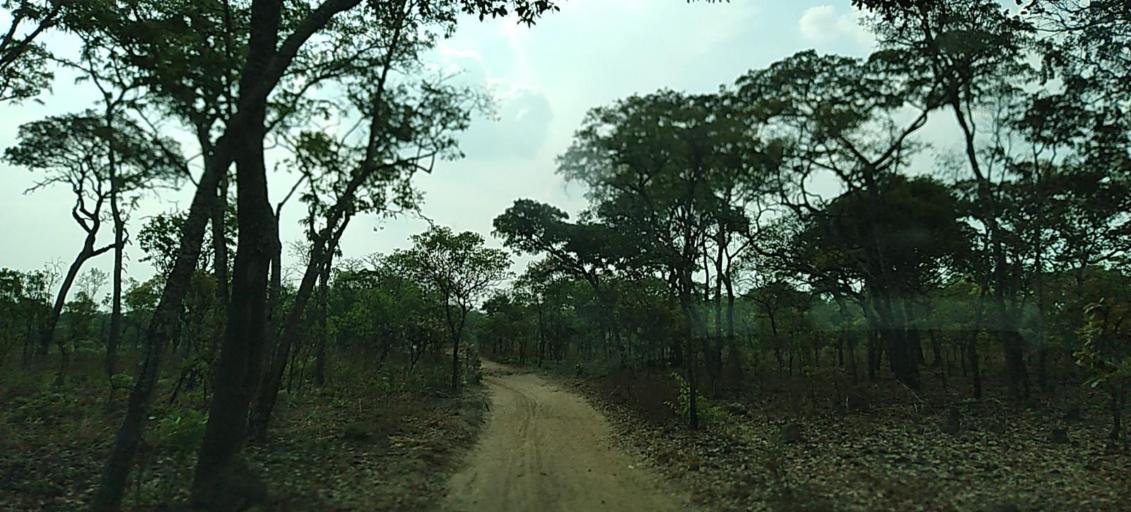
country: ZM
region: North-Western
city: Solwezi
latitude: -12.0772
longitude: 26.2417
